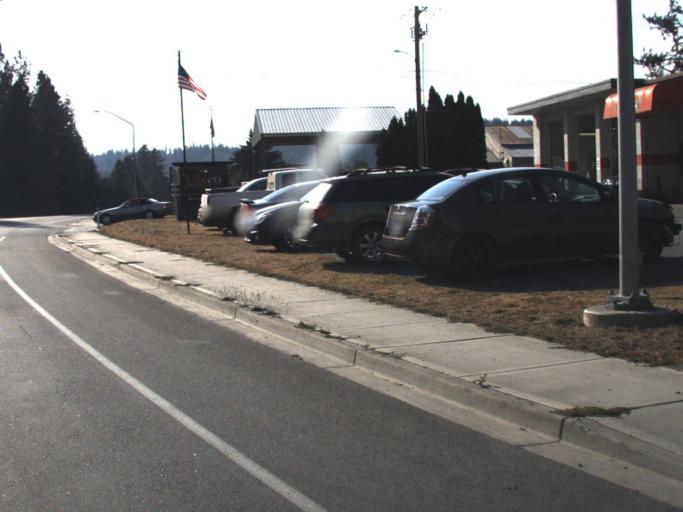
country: US
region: Washington
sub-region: Pend Oreille County
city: Newport
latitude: 48.1760
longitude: -117.0493
